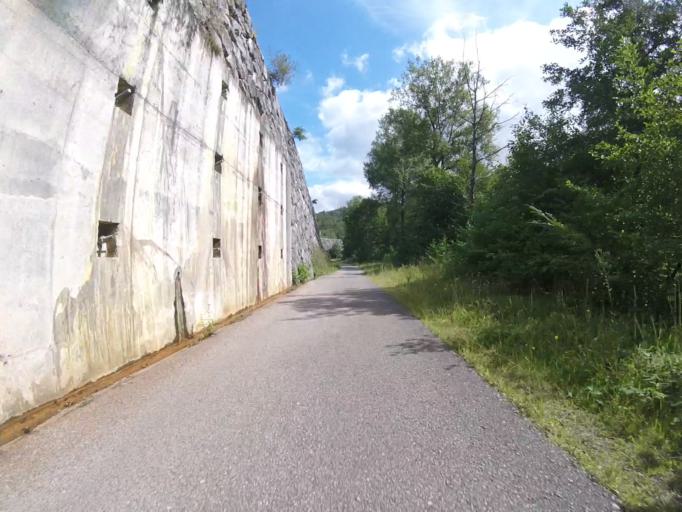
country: ES
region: Navarre
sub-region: Provincia de Navarra
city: Igantzi
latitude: 43.2368
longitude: -1.6762
